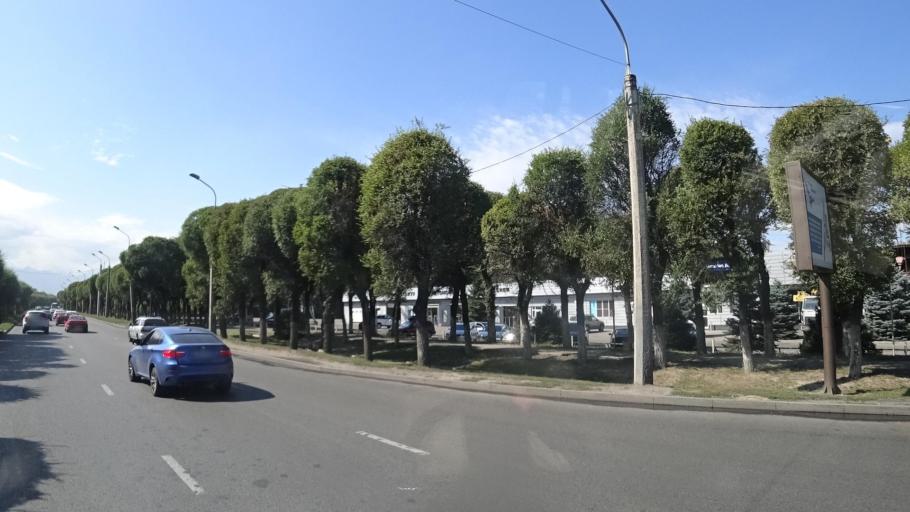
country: KZ
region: Almaty Oblysy
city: Pervomayskiy
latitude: 43.3374
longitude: 76.9823
